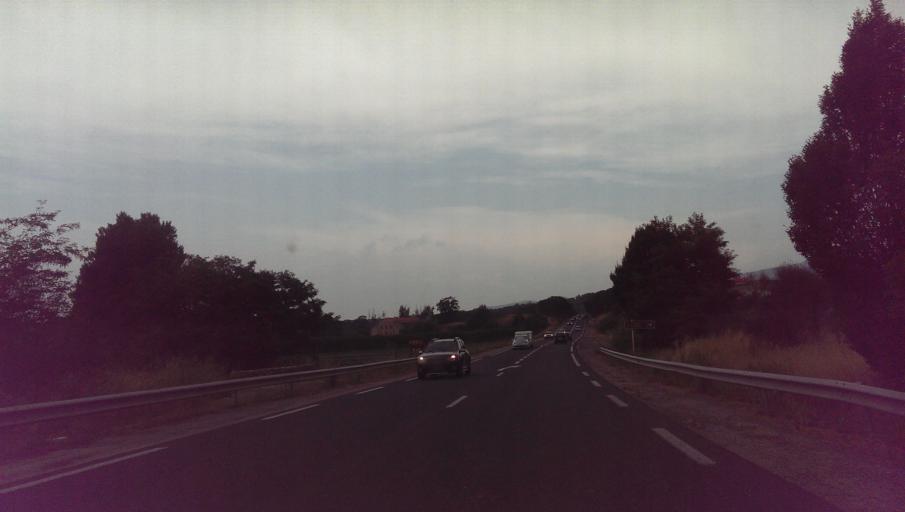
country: FR
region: Languedoc-Roussillon
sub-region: Departement des Pyrenees-Orientales
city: Prades
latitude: 42.6237
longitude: 2.4325
